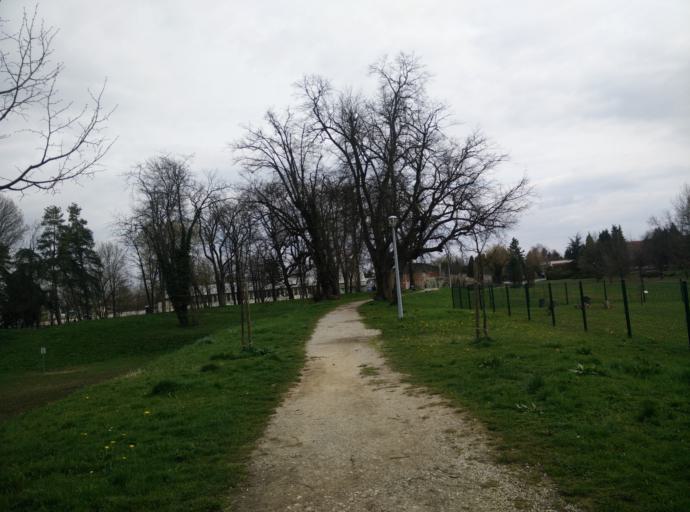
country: HR
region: Karlovacka
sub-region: Grad Karlovac
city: Karlovac
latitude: 45.4930
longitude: 15.5598
